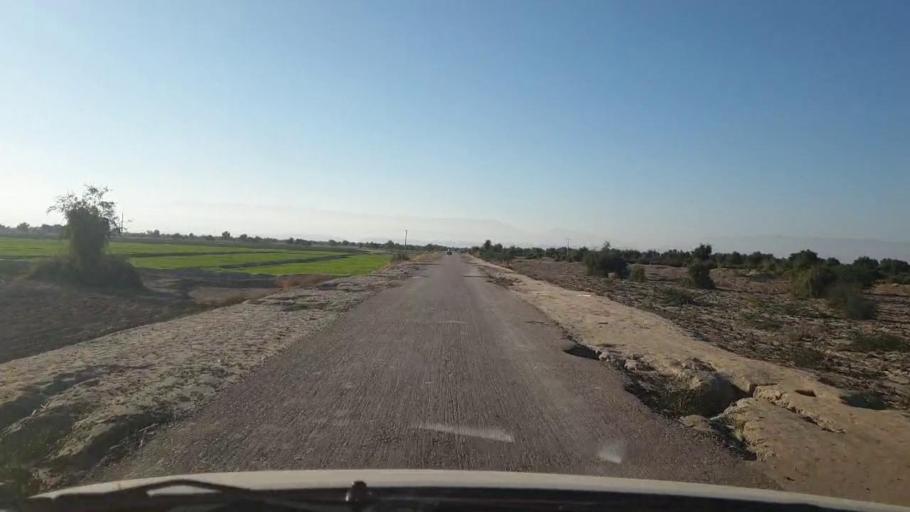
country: PK
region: Sindh
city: Johi
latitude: 26.7589
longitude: 67.4741
